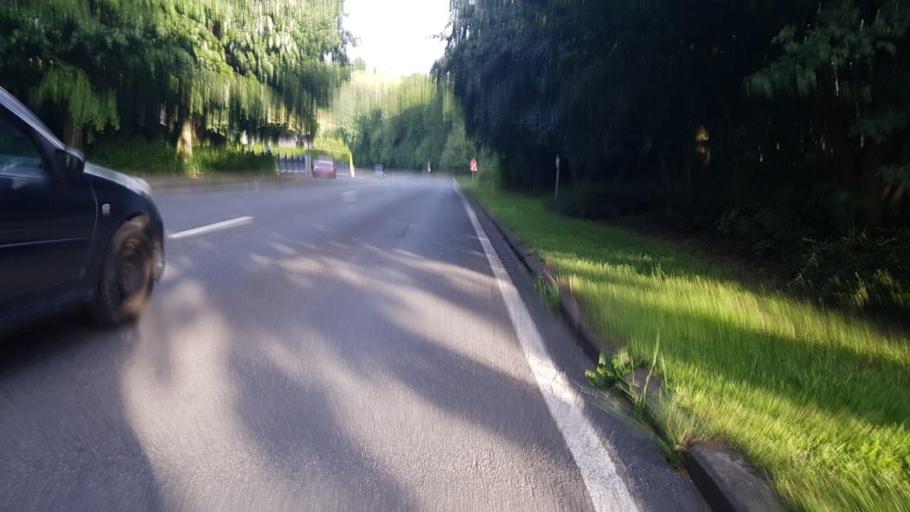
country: BE
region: Wallonia
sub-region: Province de Liege
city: Soumagne
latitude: 50.6058
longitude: 5.7192
